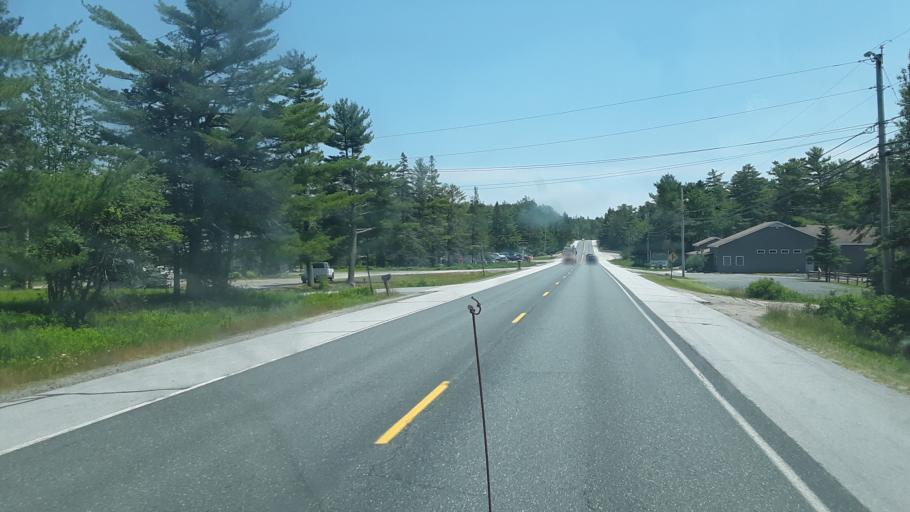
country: US
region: Maine
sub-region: Hancock County
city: Hancock
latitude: 44.5342
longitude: -68.2722
